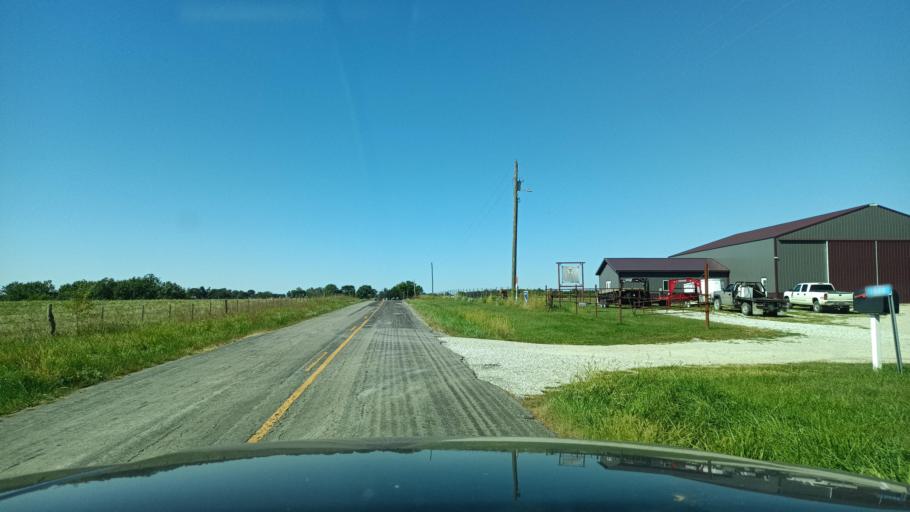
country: US
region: Missouri
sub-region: Scotland County
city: Memphis
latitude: 40.3543
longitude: -92.2882
